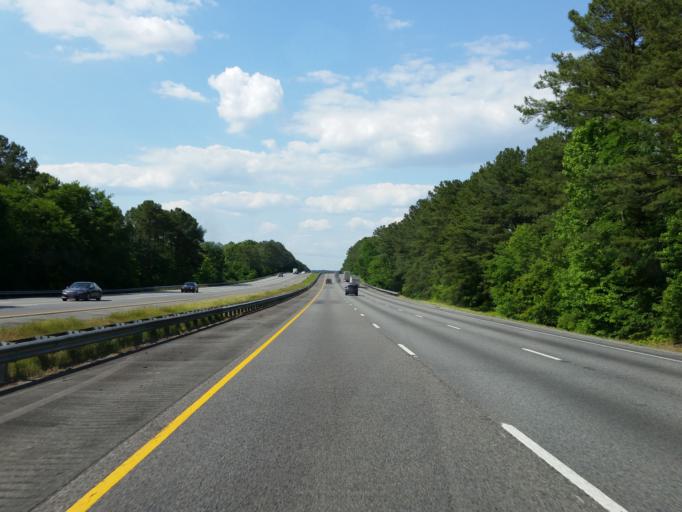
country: US
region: Georgia
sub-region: Houston County
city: Perry
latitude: 32.3920
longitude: -83.7666
